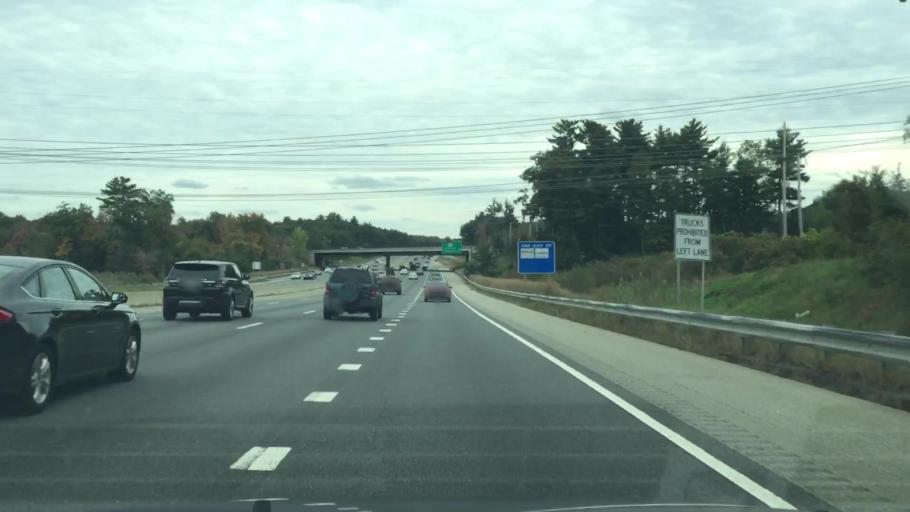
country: US
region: Massachusetts
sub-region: Middlesex County
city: Lowell
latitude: 42.5915
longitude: -71.3153
